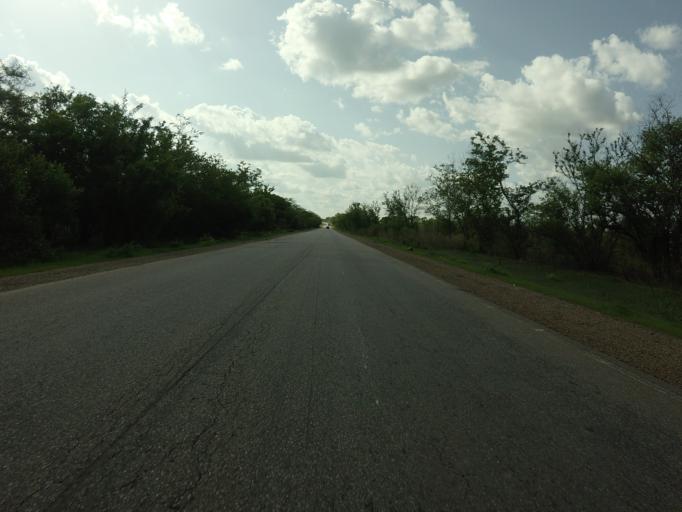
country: GH
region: Upper East
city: Bolgatanga
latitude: 10.5201
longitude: -0.8125
